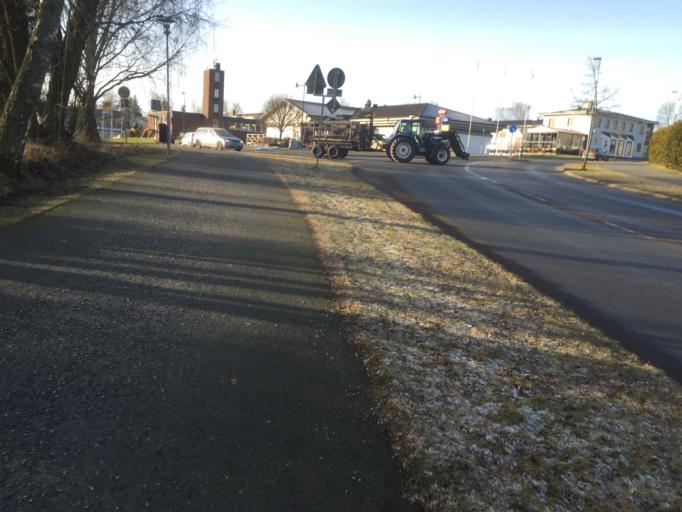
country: SE
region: Joenkoeping
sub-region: Aneby Kommun
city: Aneby
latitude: 57.8385
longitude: 14.8119
